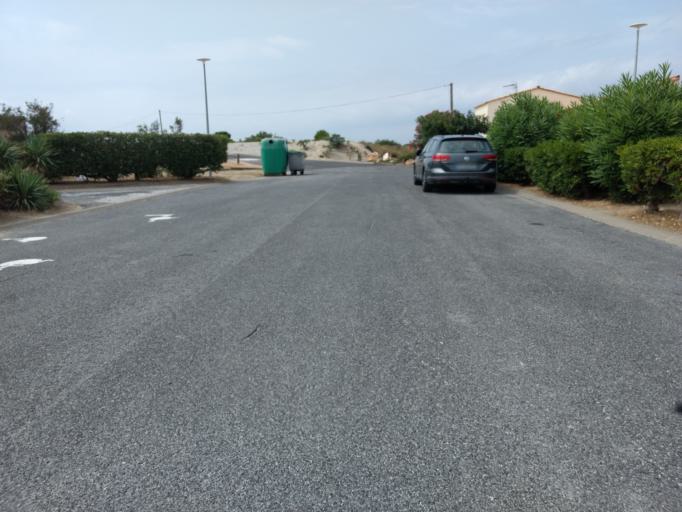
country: FR
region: Languedoc-Roussillon
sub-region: Departement des Pyrenees-Orientales
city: Le Barcares
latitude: 42.8370
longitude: 3.0372
